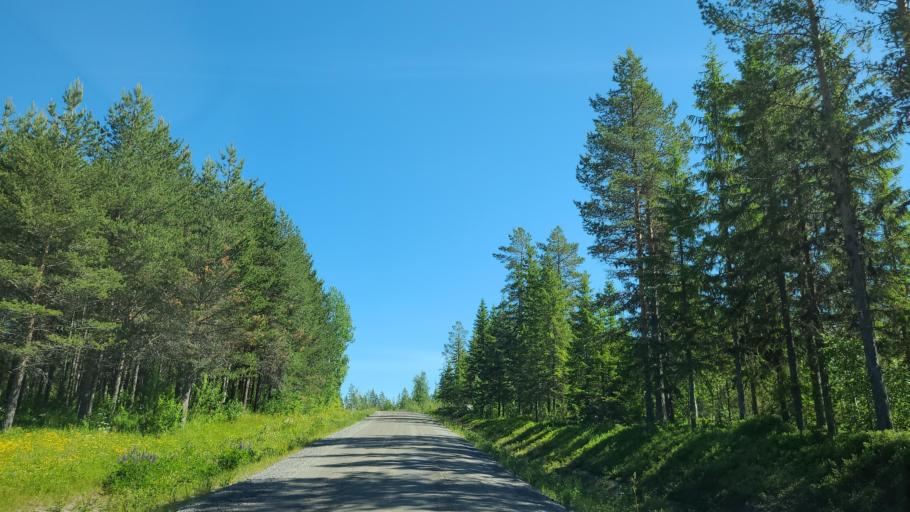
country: SE
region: Vaesterbotten
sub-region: Bjurholms Kommun
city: Bjurholm
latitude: 63.6415
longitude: 19.1025
